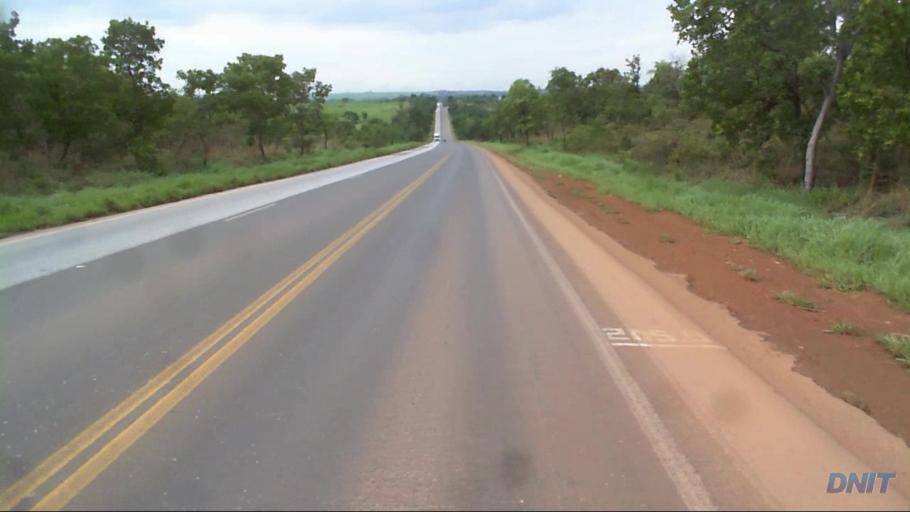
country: BR
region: Goias
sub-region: Uruacu
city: Uruacu
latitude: -14.5765
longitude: -49.1584
